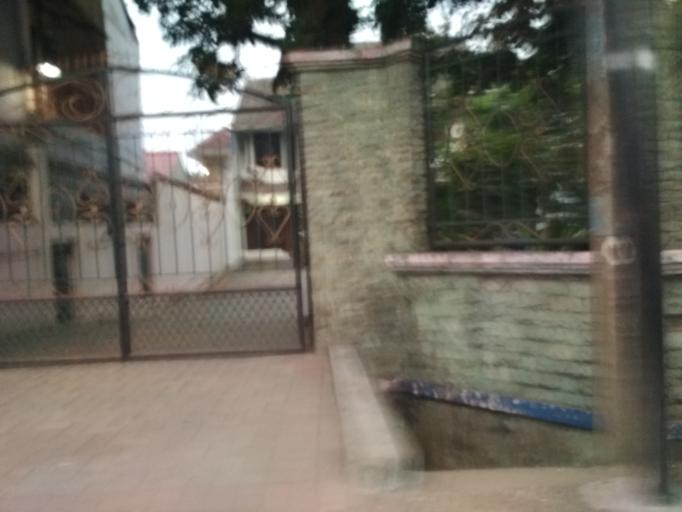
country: ID
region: West Java
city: Caringin
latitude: -6.7147
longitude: 106.8203
